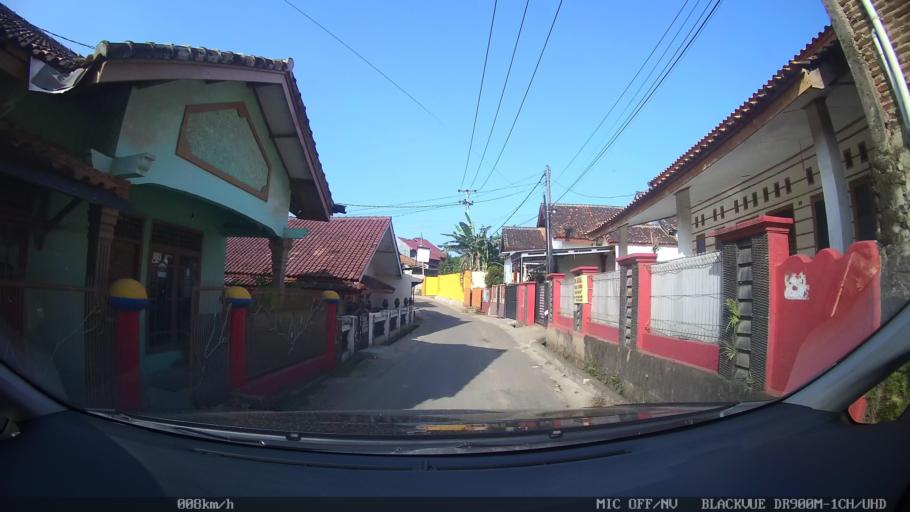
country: ID
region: Lampung
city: Kedaton
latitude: -5.3742
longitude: 105.2332
